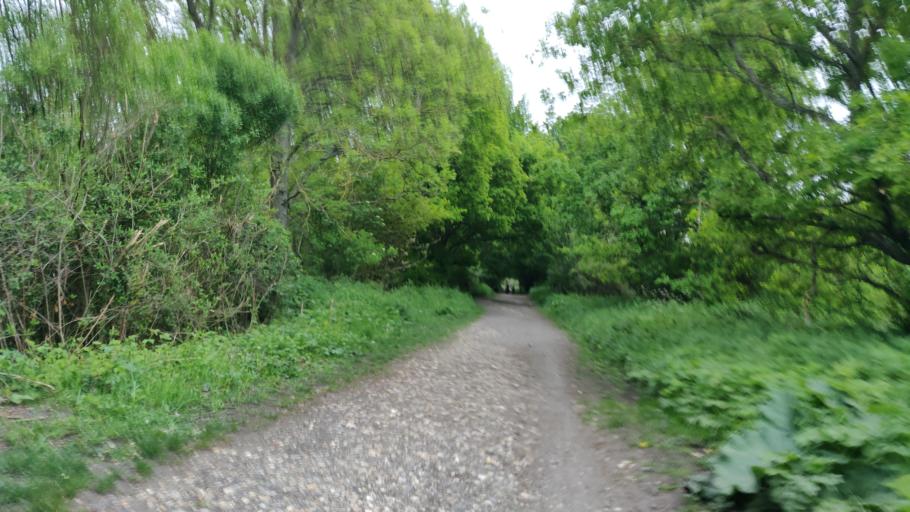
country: GB
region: England
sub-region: West Sussex
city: Partridge Green
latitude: 50.9978
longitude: -0.3182
